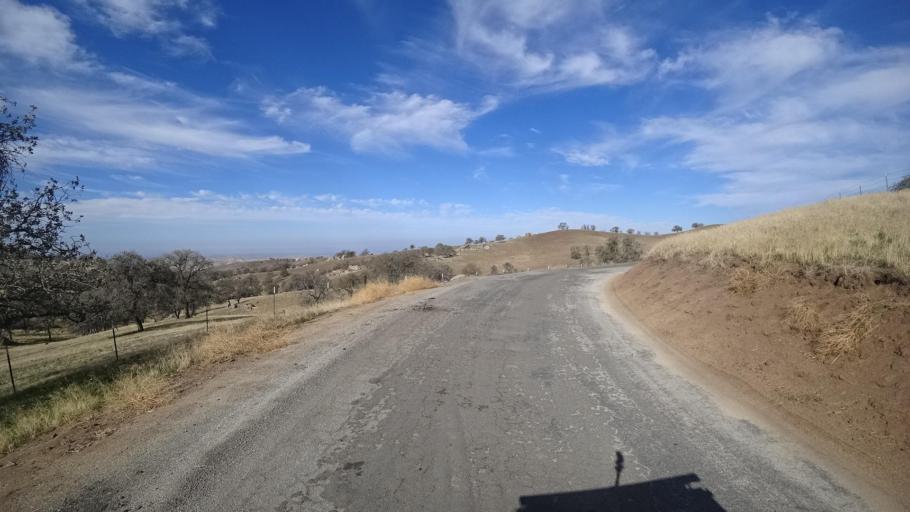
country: US
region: California
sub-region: Kern County
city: Oildale
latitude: 35.5886
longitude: -118.8268
